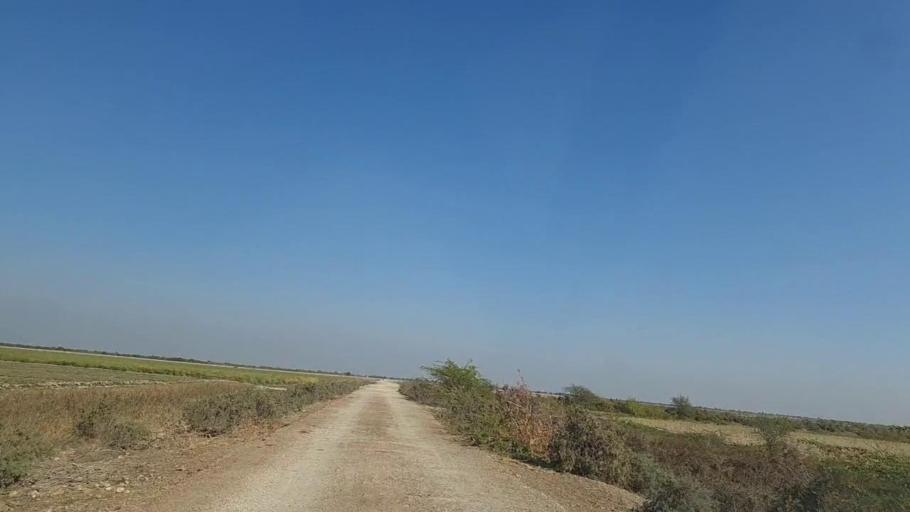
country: PK
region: Sindh
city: Samaro
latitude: 25.3990
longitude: 69.4305
